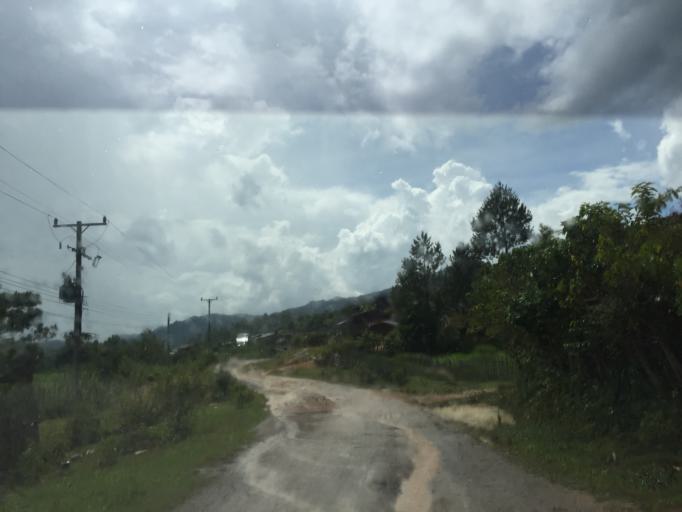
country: LA
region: Xiangkhoang
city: Muang Phonsavan
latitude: 19.3406
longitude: 103.5669
